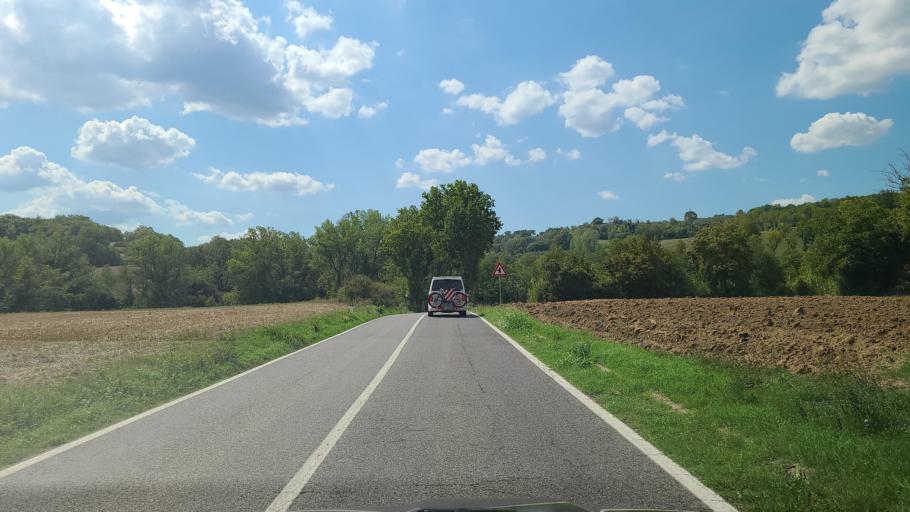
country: IT
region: Tuscany
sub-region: Provincia di Siena
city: Colle di Val d'Elsa
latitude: 43.4112
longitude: 11.0698
